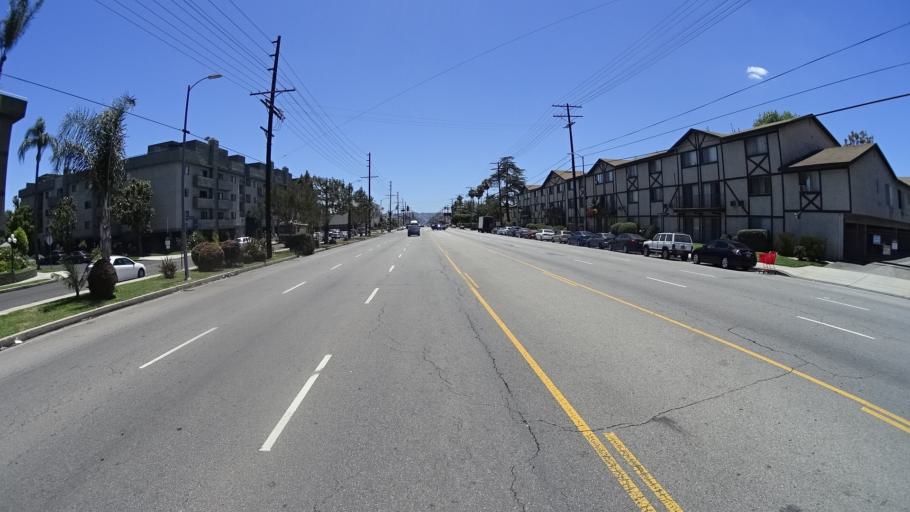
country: US
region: California
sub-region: Los Angeles County
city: Van Nuys
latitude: 34.2060
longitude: -118.4662
